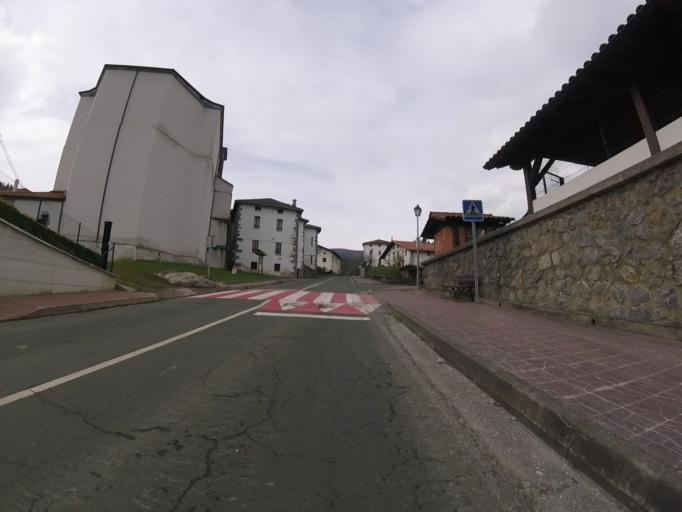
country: ES
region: Basque Country
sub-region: Provincia de Guipuzcoa
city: Errezil
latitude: 43.1423
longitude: -2.1670
